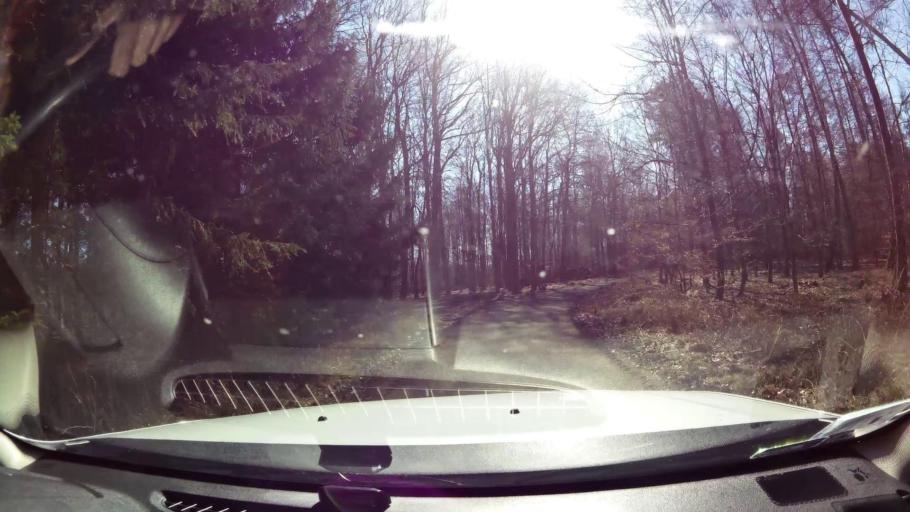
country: PL
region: West Pomeranian Voivodeship
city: Trzcinsko Zdroj
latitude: 53.0274
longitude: 14.6357
